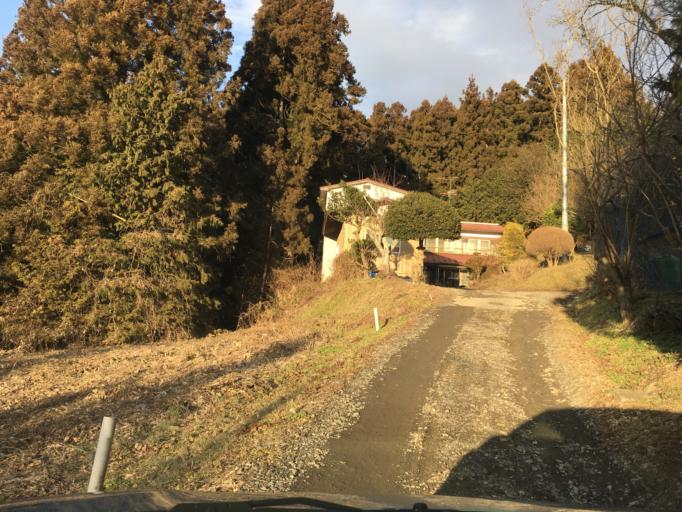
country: JP
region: Iwate
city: Ichinoseki
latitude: 38.8535
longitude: 141.2905
